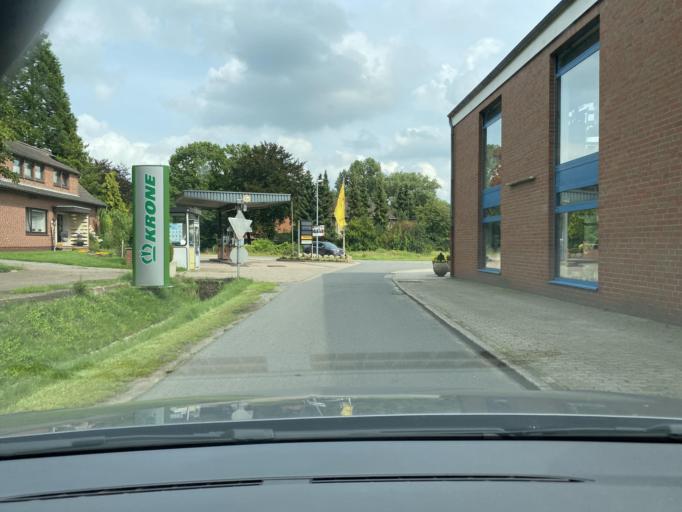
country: DE
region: Lower Saxony
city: Vollersode
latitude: 53.3254
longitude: 8.9109
